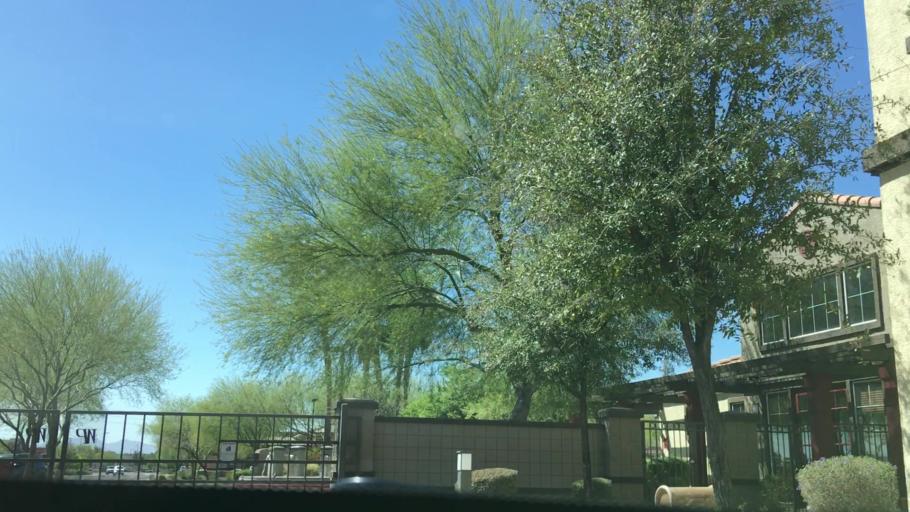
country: US
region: Arizona
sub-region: Maricopa County
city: Peoria
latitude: 33.6122
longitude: -112.2345
